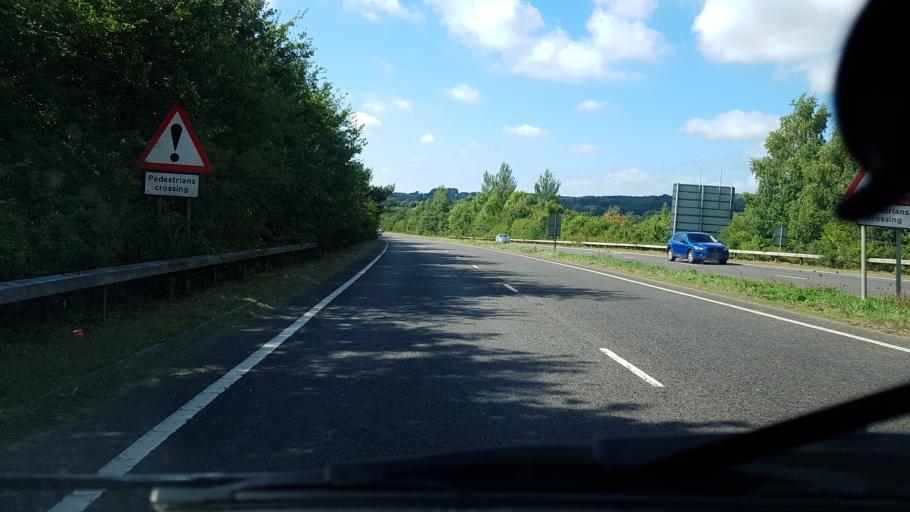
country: GB
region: England
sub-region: West Sussex
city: Horsham
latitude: 51.0850
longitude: -0.2924
